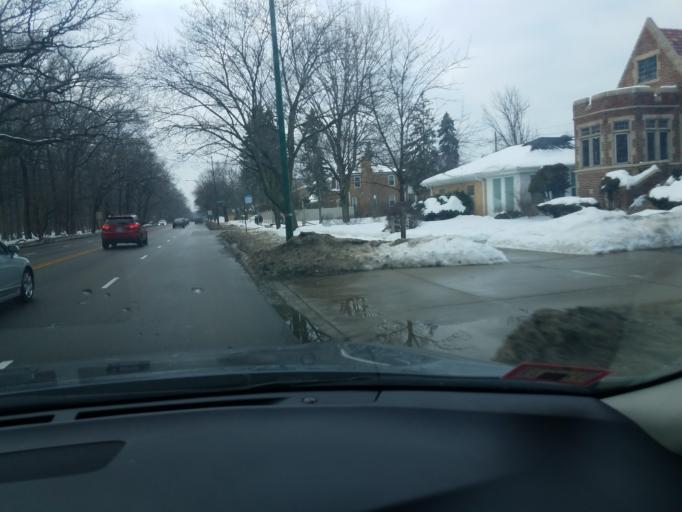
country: US
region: Illinois
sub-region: Cook County
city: Niles
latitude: 41.9990
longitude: -87.7702
